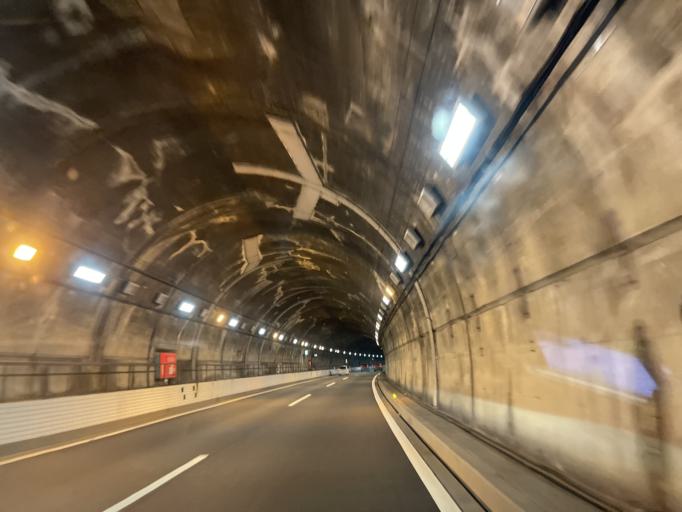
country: JP
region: Nagano
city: Okaya
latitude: 36.0601
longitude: 138.0364
